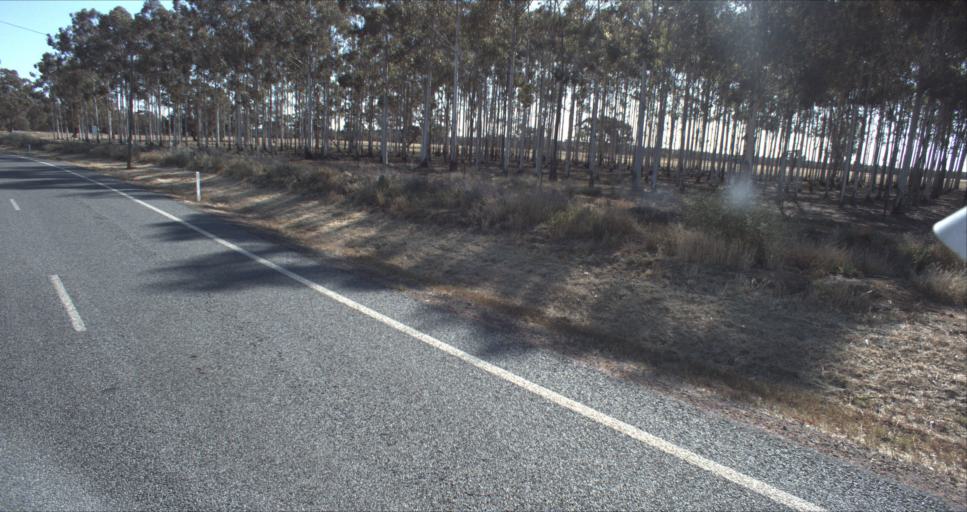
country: AU
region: New South Wales
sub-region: Leeton
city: Leeton
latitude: -34.6221
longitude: 146.3962
